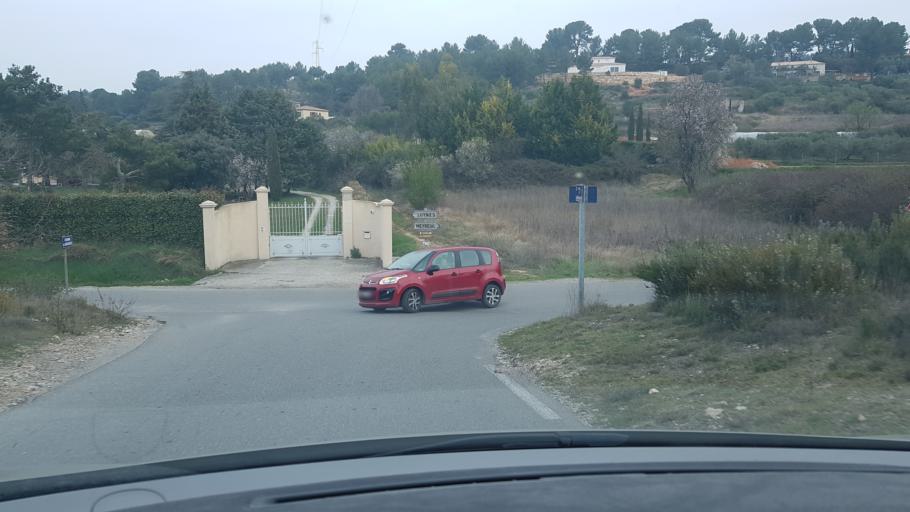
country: FR
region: Provence-Alpes-Cote d'Azur
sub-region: Departement des Bouches-du-Rhone
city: Meyreuil
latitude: 43.4820
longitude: 5.4816
